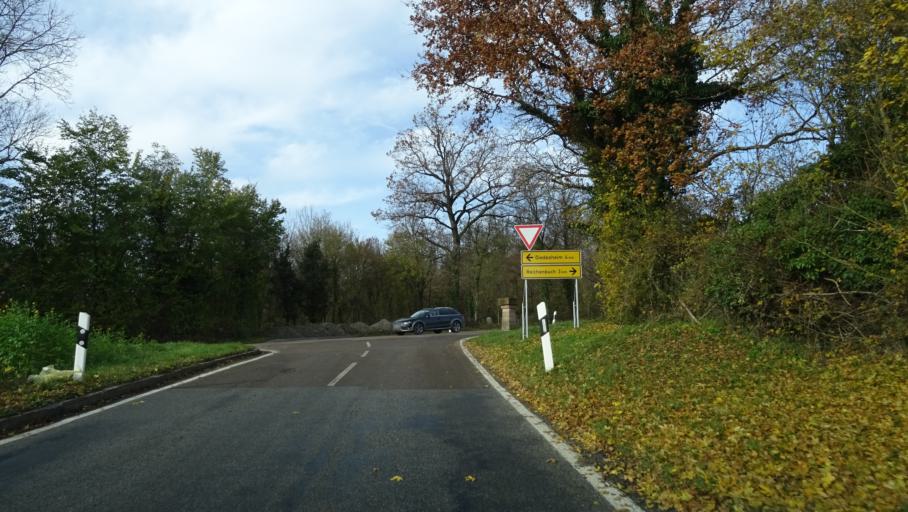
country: DE
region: Baden-Wuerttemberg
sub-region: Karlsruhe Region
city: Obrigheim
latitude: 49.3729
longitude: 9.1136
